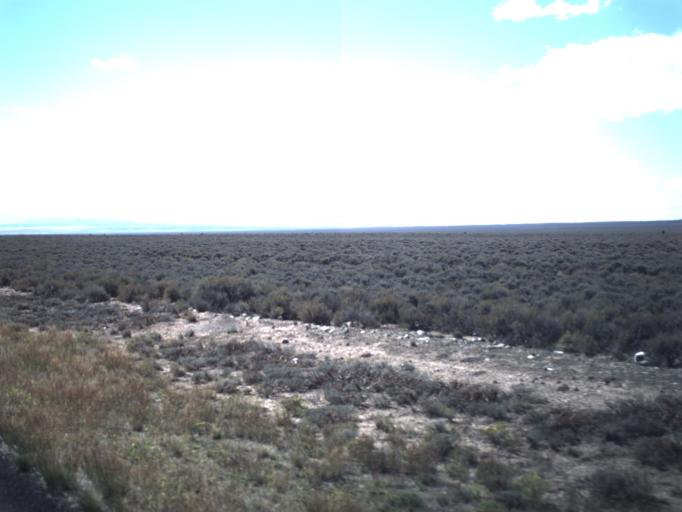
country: US
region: Utah
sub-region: Iron County
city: Enoch
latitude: 37.9959
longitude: -112.9995
